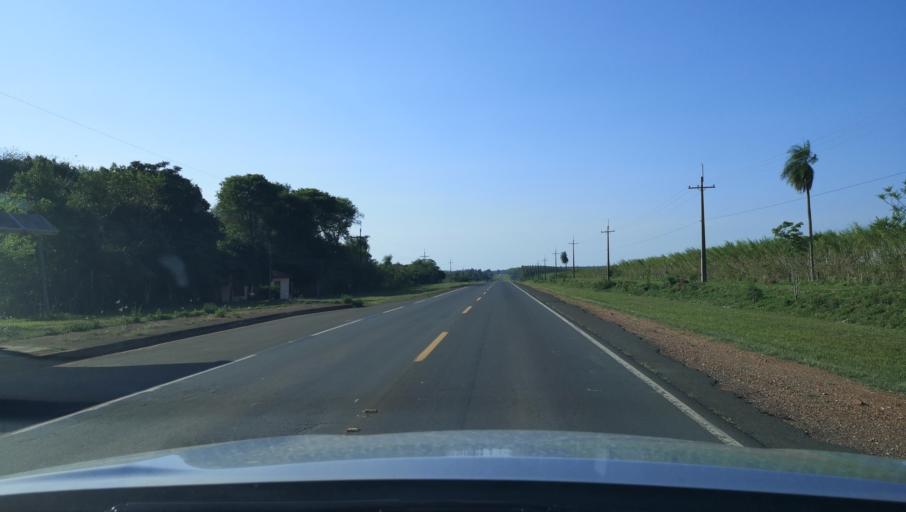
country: PY
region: Misiones
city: Santa Maria
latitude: -26.7819
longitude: -57.0273
